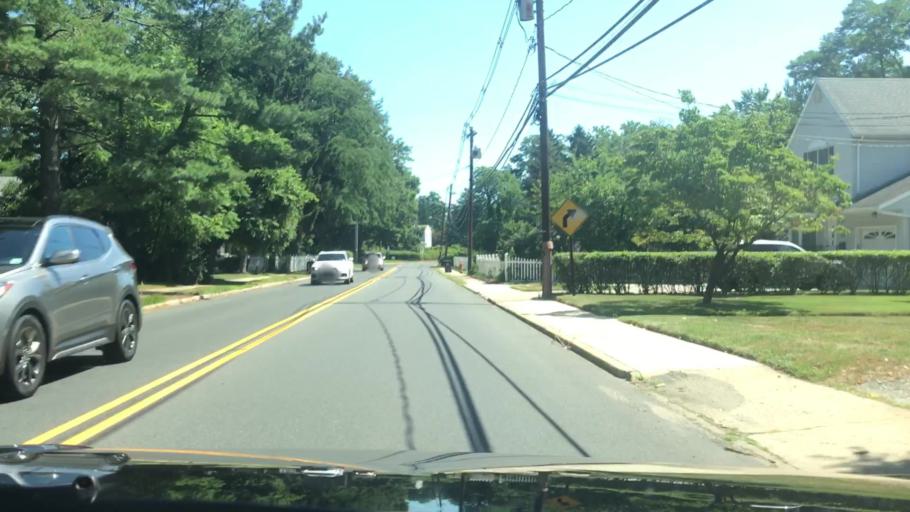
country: US
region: New Jersey
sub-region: Monmouth County
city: Red Bank
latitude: 40.3475
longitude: -74.0872
